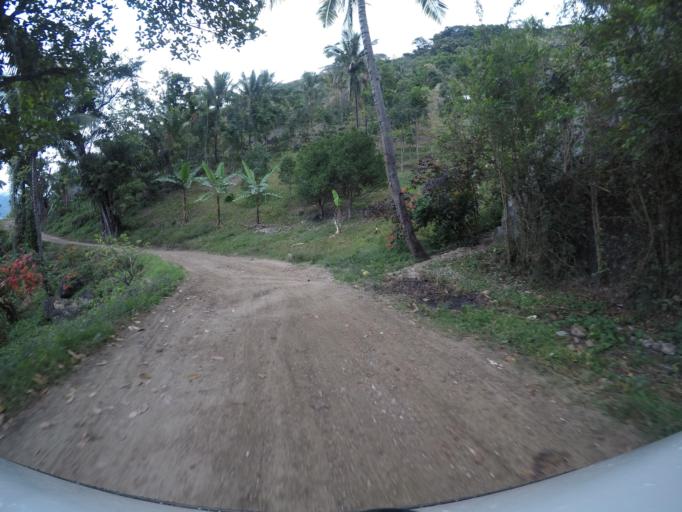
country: TL
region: Baucau
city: Baucau
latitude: -8.6434
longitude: 126.6344
